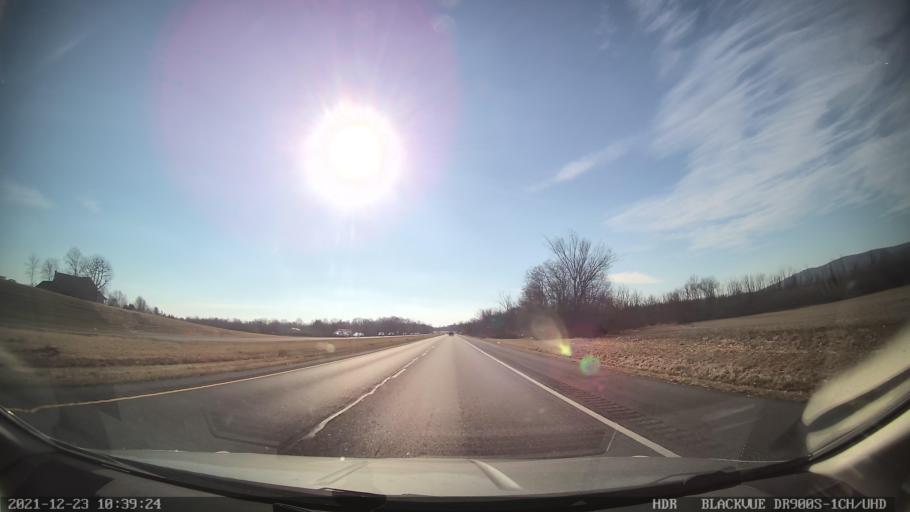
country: US
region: Maryland
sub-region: Frederick County
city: Thurmont
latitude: 39.5415
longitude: -77.4255
